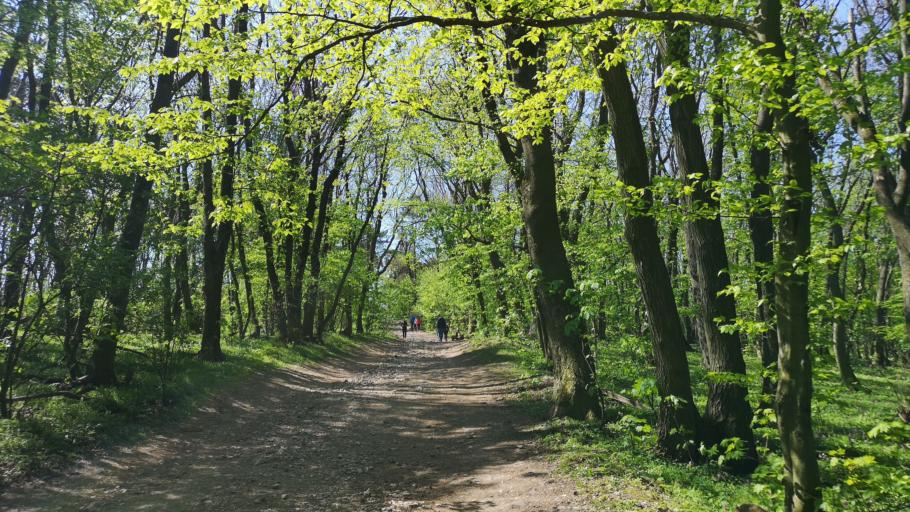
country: SK
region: Nitriansky
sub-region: Okres Nitra
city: Nitra
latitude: 48.3443
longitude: 18.1057
